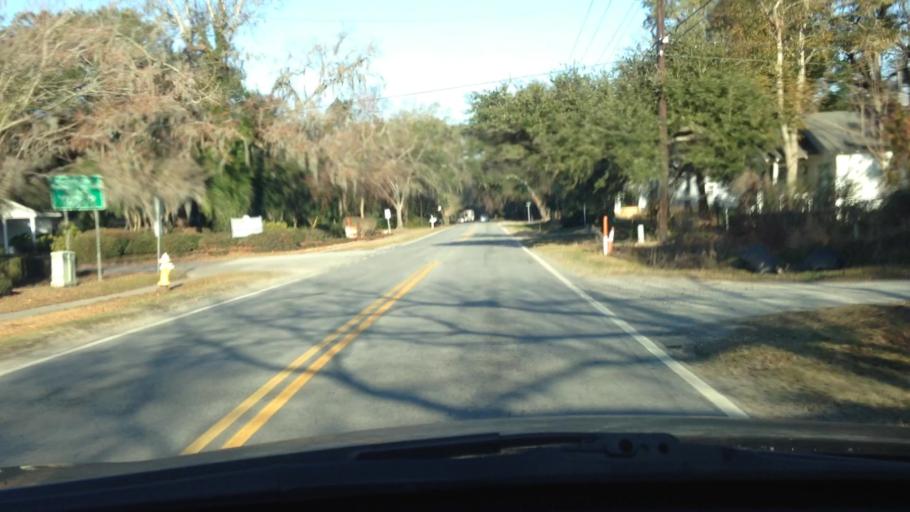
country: US
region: South Carolina
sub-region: Charleston County
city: Charleston
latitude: 32.7469
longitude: -79.9874
